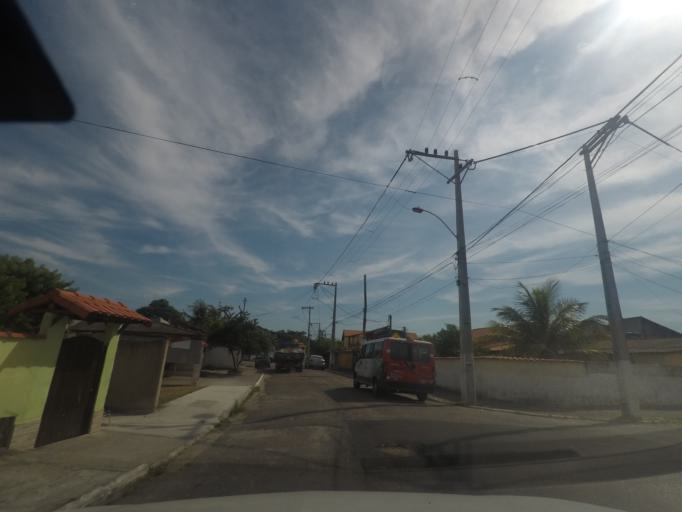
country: BR
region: Rio de Janeiro
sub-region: Marica
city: Marica
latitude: -22.9553
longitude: -42.8107
